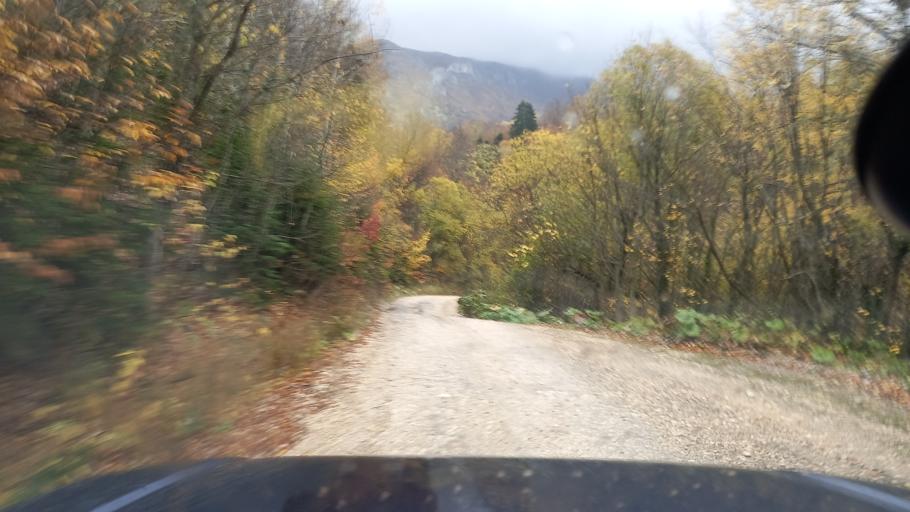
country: RU
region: Krasnodarskiy
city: Neftegorsk
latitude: 44.0190
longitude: 39.8438
